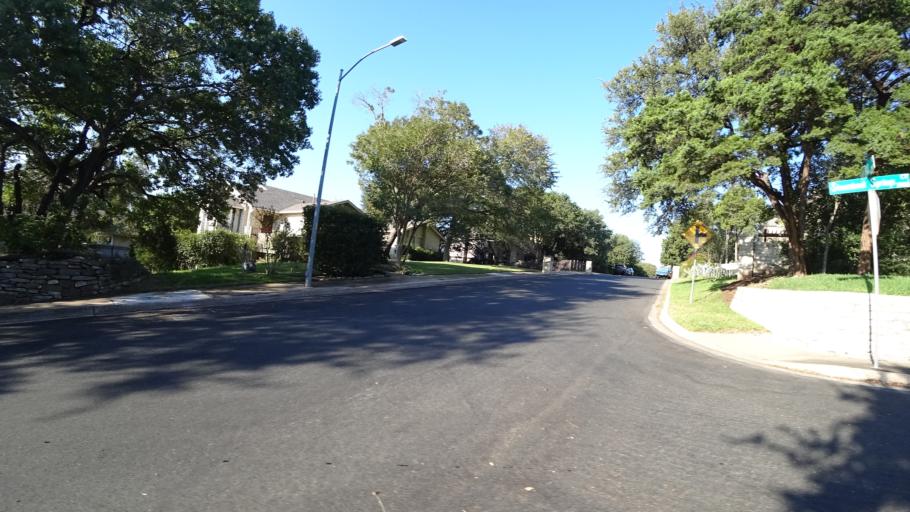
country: US
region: Texas
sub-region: Travis County
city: Rollingwood
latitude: 30.2607
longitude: -97.8001
